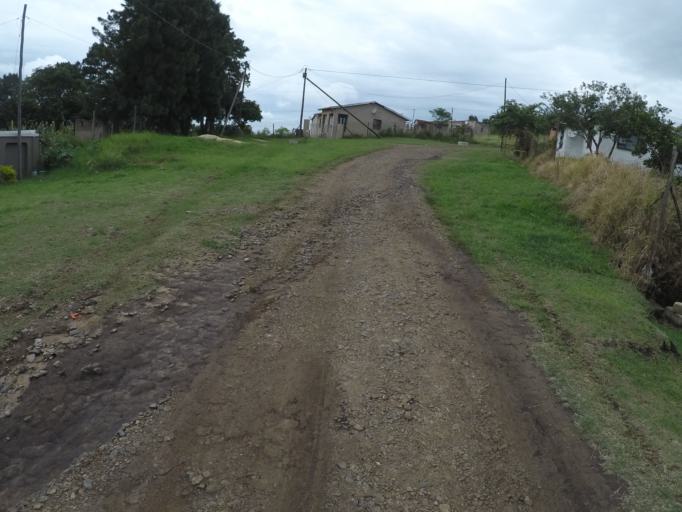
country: ZA
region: KwaZulu-Natal
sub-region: uThungulu District Municipality
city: Empangeni
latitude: -28.7840
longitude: 31.8593
